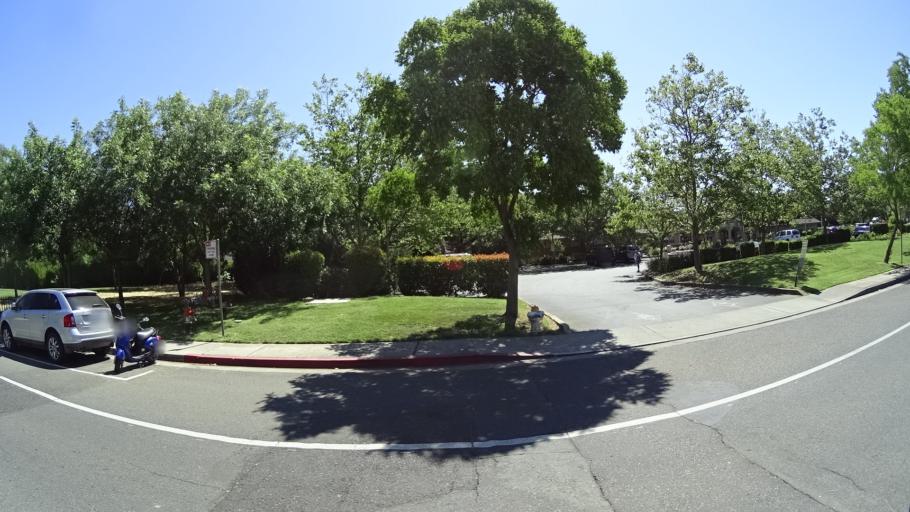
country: US
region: California
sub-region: Sacramento County
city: Sacramento
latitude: 38.5520
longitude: -121.4480
